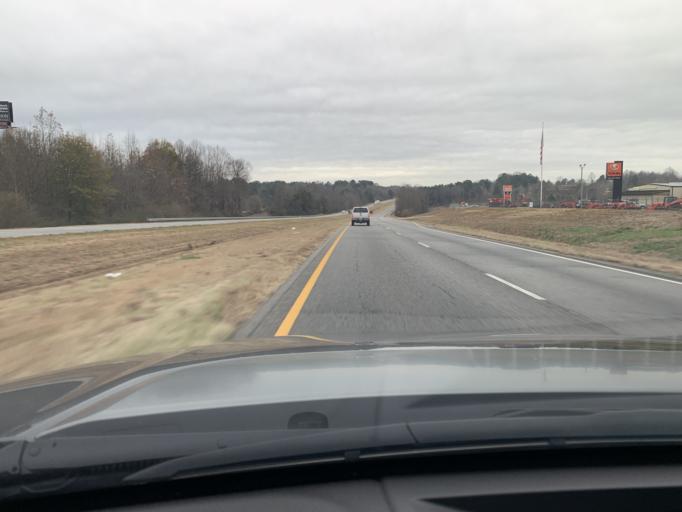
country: US
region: Georgia
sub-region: Habersham County
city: Raoul
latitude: 34.4560
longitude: -83.6106
